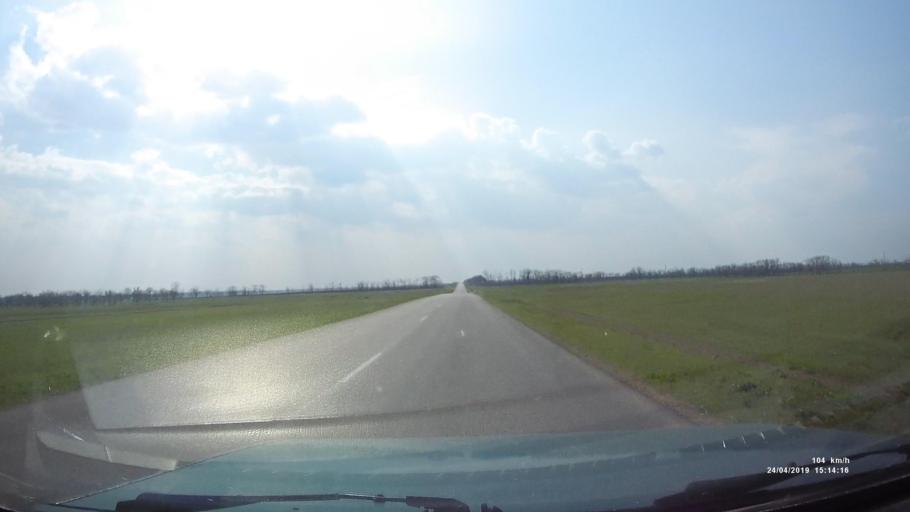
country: RU
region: Rostov
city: Remontnoye
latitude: 46.5464
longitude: 43.2623
